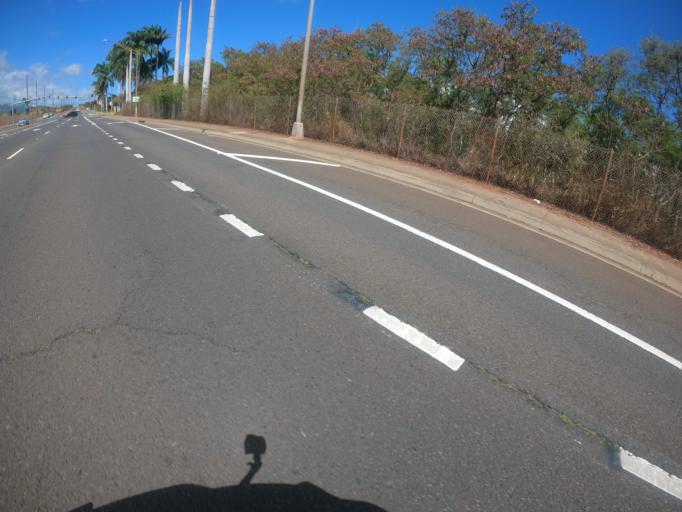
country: US
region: Hawaii
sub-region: Honolulu County
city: Village Park
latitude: 21.3956
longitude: -158.0375
